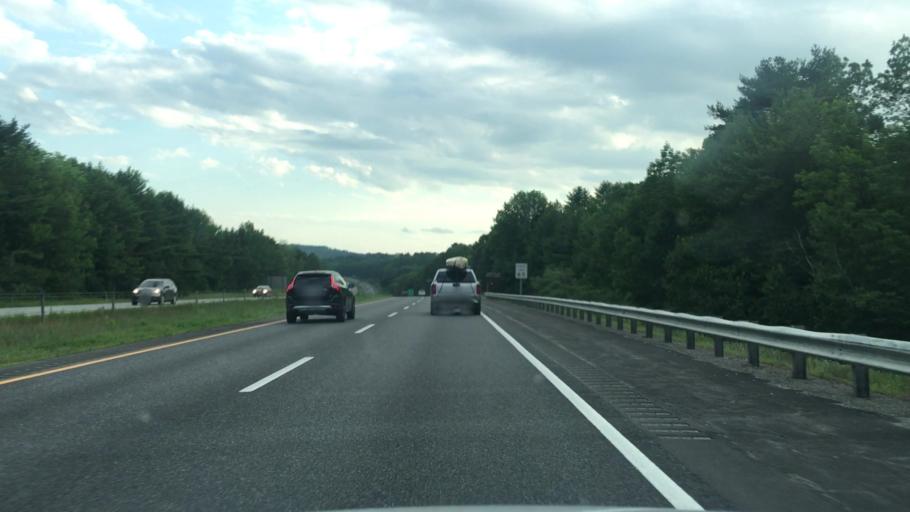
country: US
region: Maine
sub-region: Kennebec County
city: Augusta
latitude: 44.3432
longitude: -69.8002
